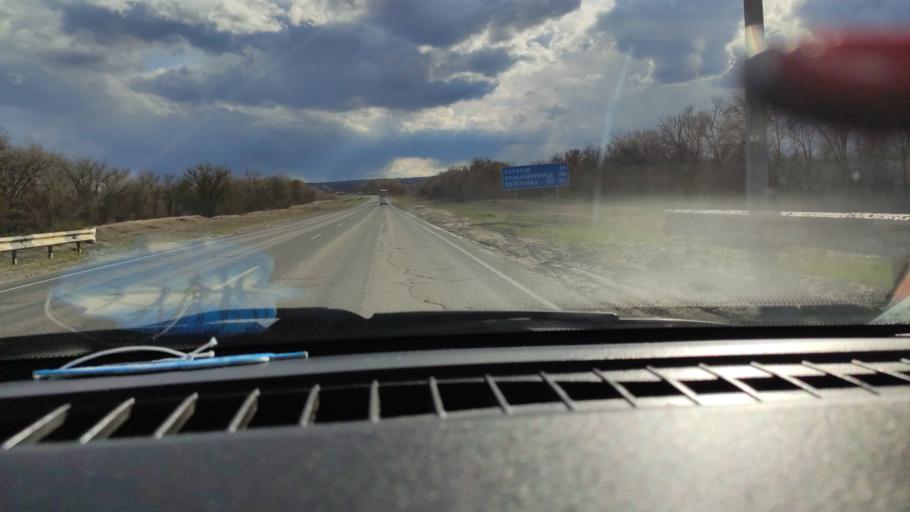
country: RU
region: Saratov
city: Sinodskoye
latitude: 51.9776
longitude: 46.6501
